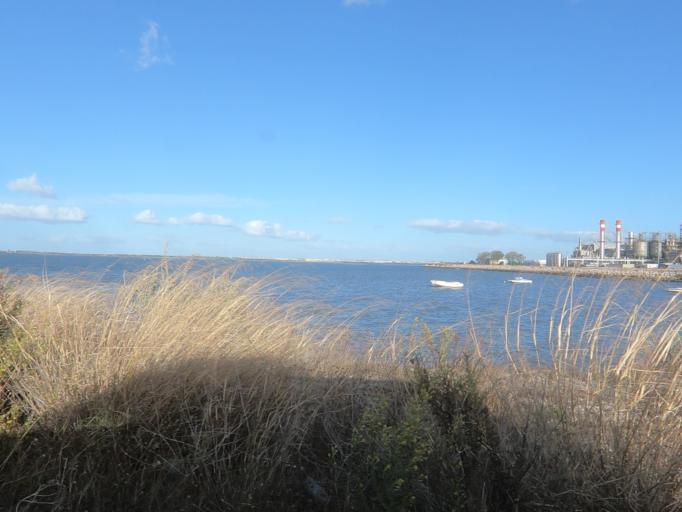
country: PT
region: Setubal
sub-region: Barreiro
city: Barreiro
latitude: 38.6782
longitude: -9.0549
